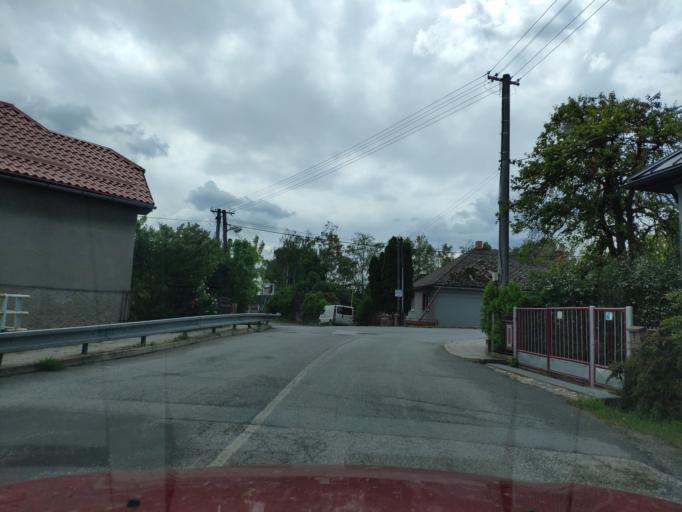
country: SK
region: Kosicky
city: Kosice
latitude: 48.8481
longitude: 21.3171
